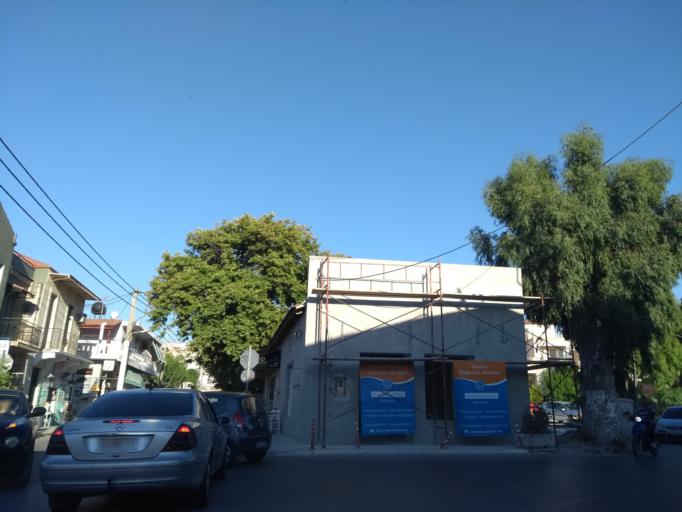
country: GR
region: Crete
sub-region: Nomos Chanias
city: Kalivai
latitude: 35.4516
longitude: 24.1742
